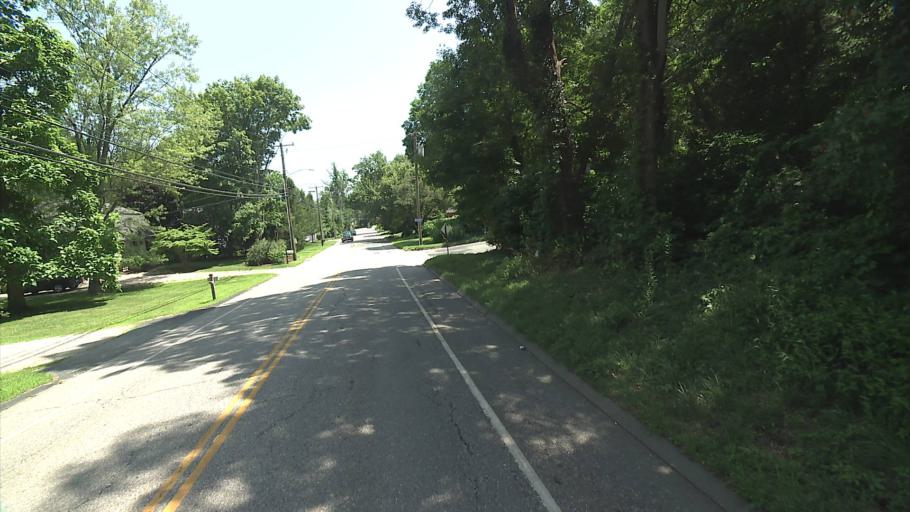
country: US
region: Connecticut
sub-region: Middlesex County
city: Essex Village
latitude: 41.3482
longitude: -72.3966
